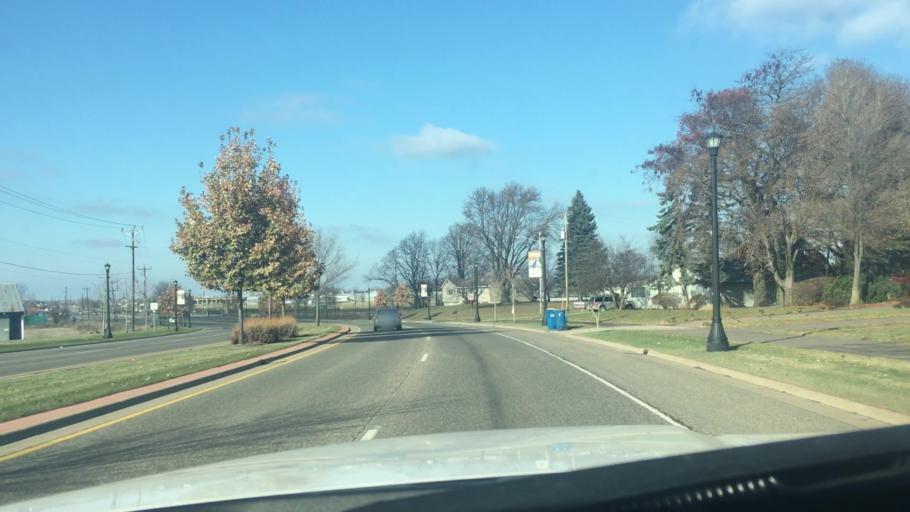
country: US
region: Minnesota
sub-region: Washington County
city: Hugo
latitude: 45.1602
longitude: -92.9999
